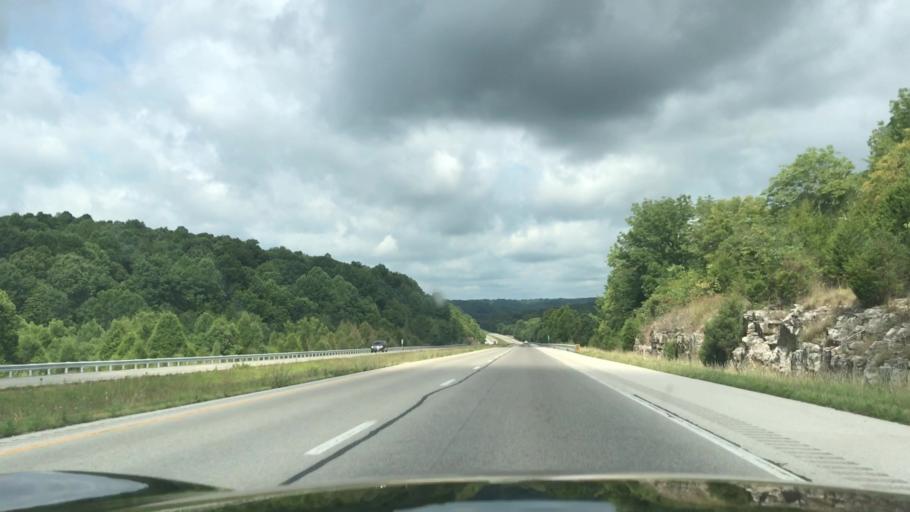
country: US
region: Kentucky
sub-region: Warren County
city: Bowling Green
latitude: 37.0375
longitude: -86.5548
